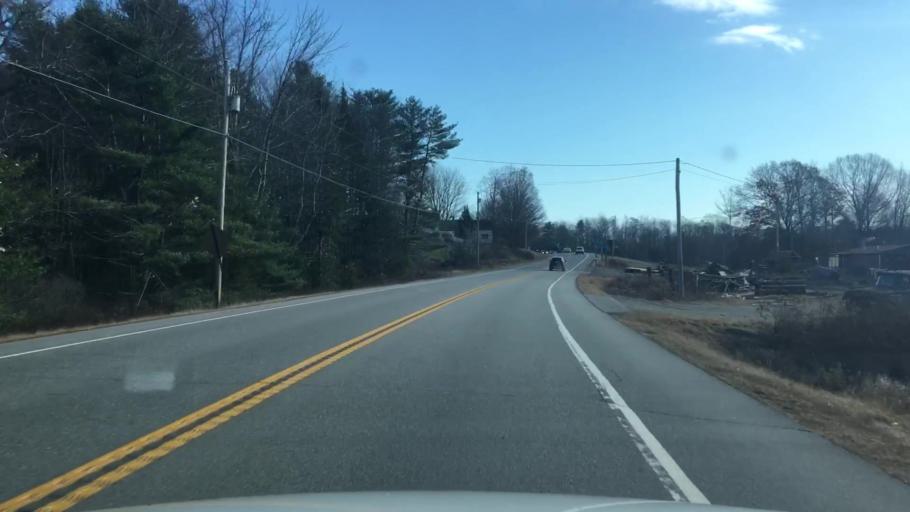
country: US
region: Maine
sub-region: Lincoln County
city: Jefferson
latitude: 44.2579
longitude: -69.4482
